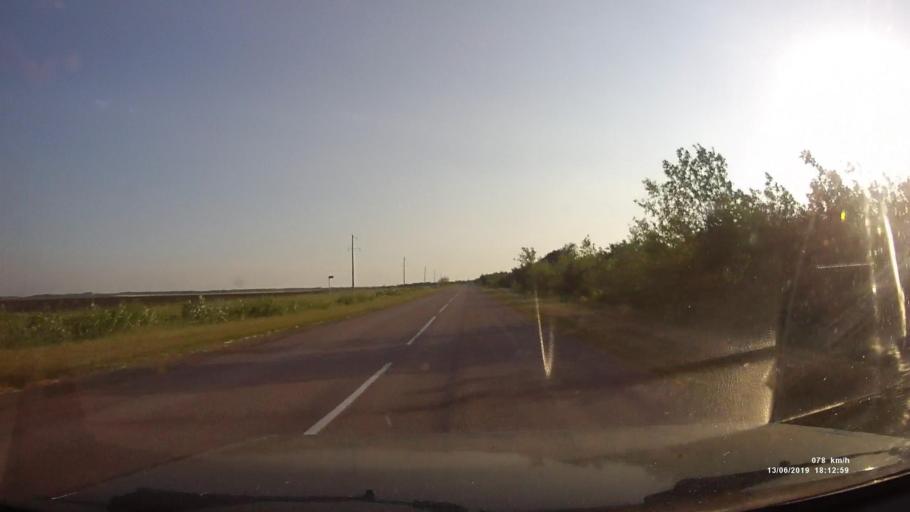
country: RU
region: Rostov
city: Kazanskaya
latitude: 49.9419
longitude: 41.4019
